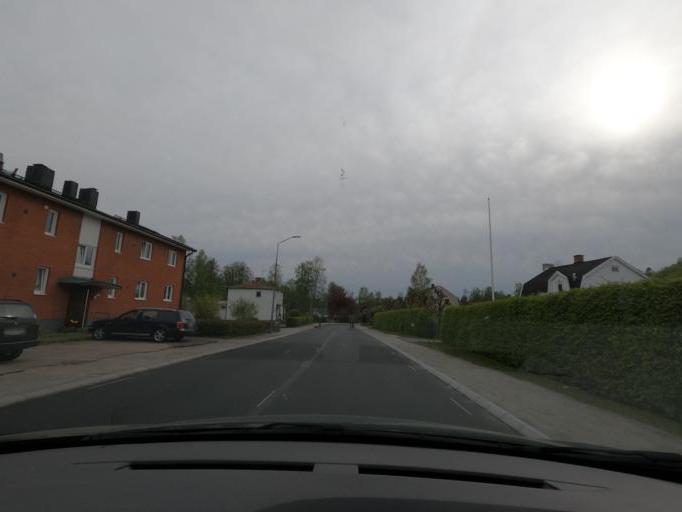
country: SE
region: Joenkoeping
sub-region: Varnamo Kommun
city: Bredaryd
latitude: 57.2200
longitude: 13.7819
